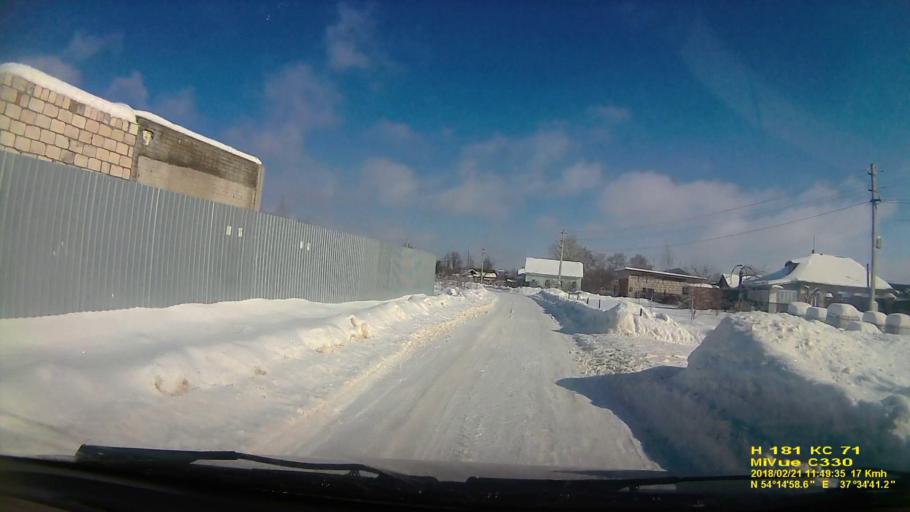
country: RU
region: Tula
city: Gorelki
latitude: 54.2502
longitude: 37.5795
